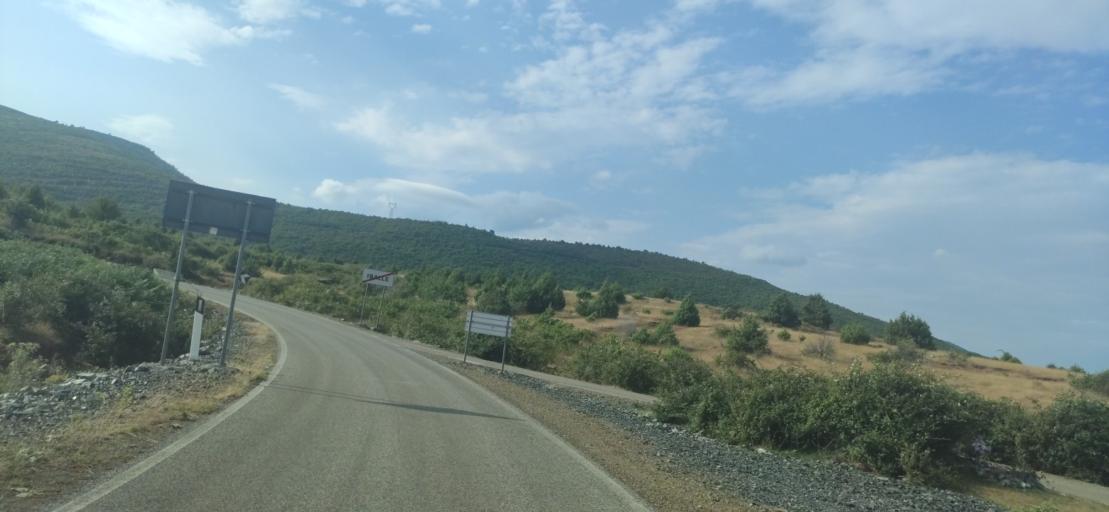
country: AL
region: Shkoder
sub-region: Rrethi i Pukes
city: Iballe
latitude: 42.1832
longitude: 19.9937
